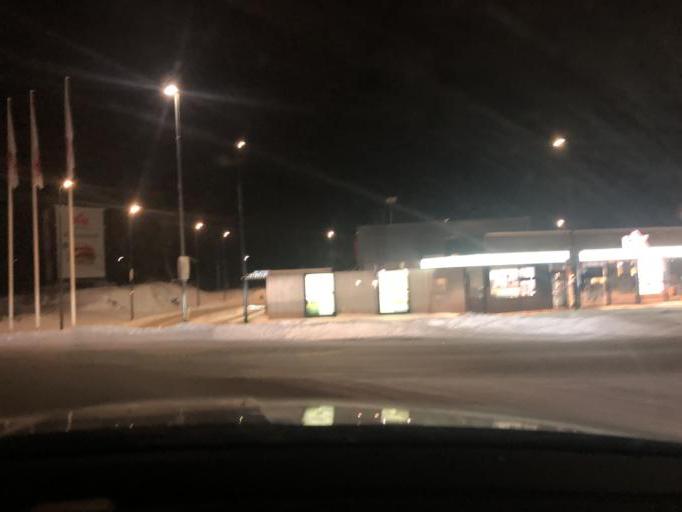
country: SE
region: Uppsala
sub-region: Uppsala Kommun
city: Saevja
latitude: 59.8438
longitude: 17.7111
